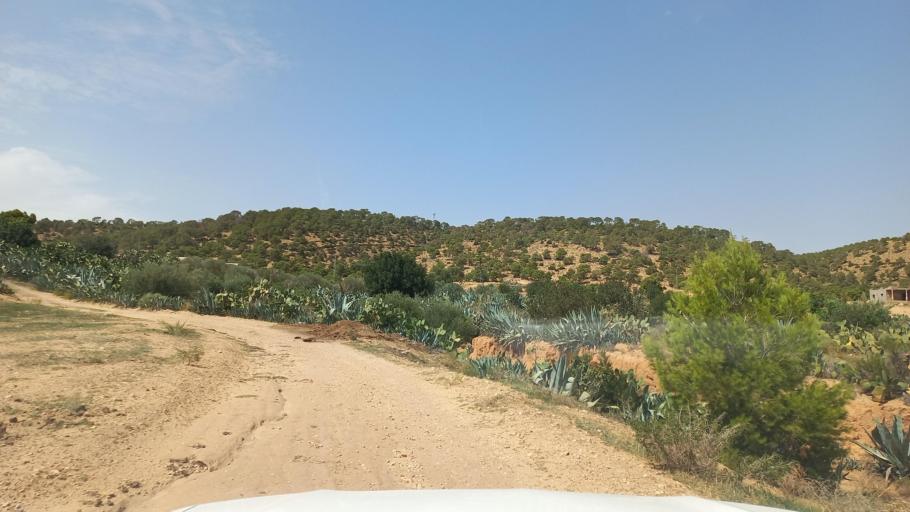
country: TN
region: Al Qasrayn
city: Kasserine
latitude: 35.3787
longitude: 8.9122
